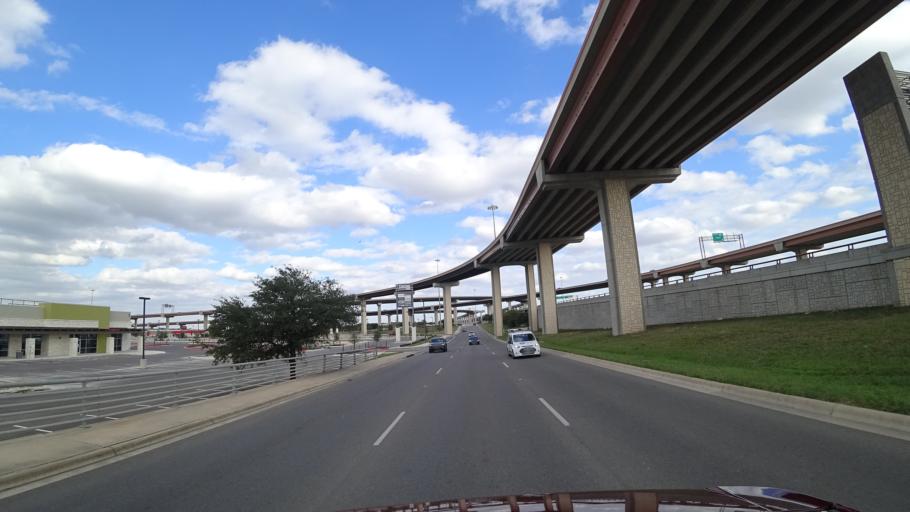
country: US
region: Texas
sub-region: Williamson County
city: Round Rock
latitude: 30.4805
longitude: -97.6780
